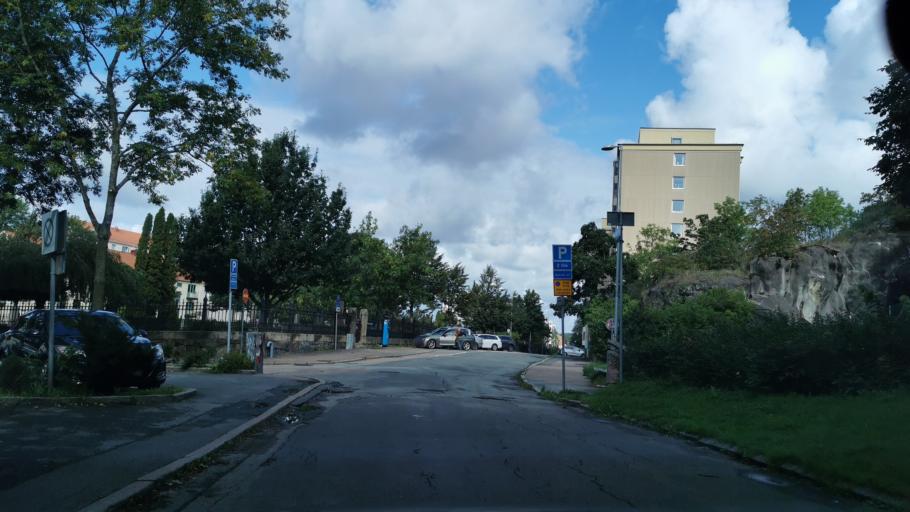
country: SE
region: Vaestra Goetaland
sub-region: Goteborg
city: Majorna
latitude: 57.6919
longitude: 11.9373
